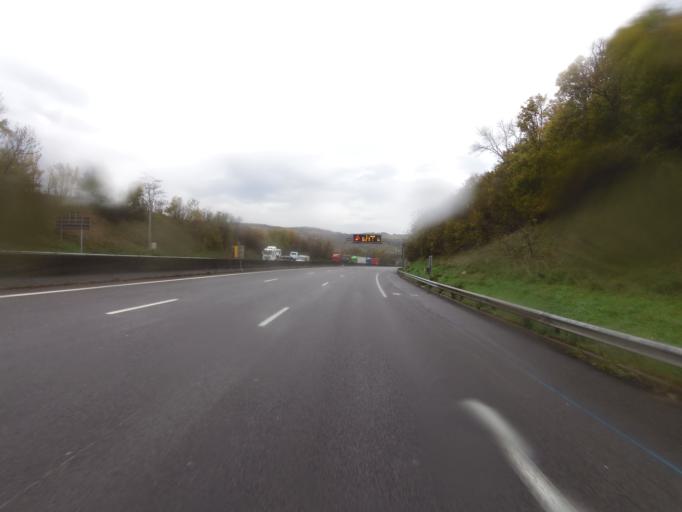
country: FR
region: Rhone-Alpes
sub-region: Departement du Rhone
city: Ampuis
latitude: 45.4893
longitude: 4.8327
